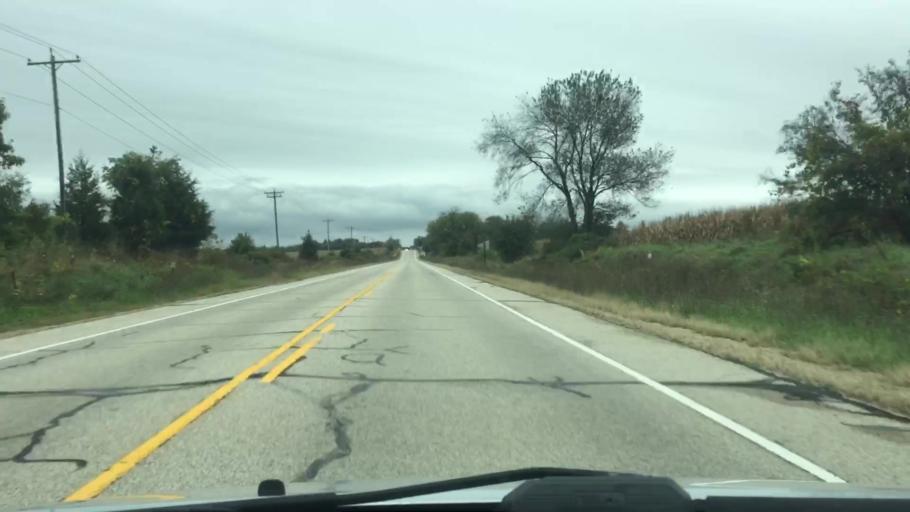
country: US
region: Wisconsin
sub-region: Jefferson County
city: Palmyra
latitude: 42.8075
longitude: -88.5626
